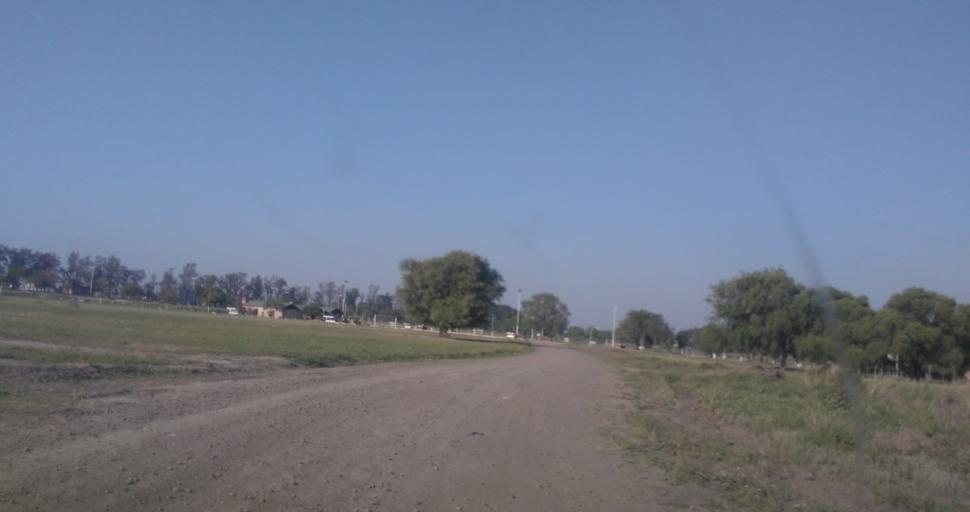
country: AR
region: Chaco
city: Fontana
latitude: -27.4378
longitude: -59.0315
